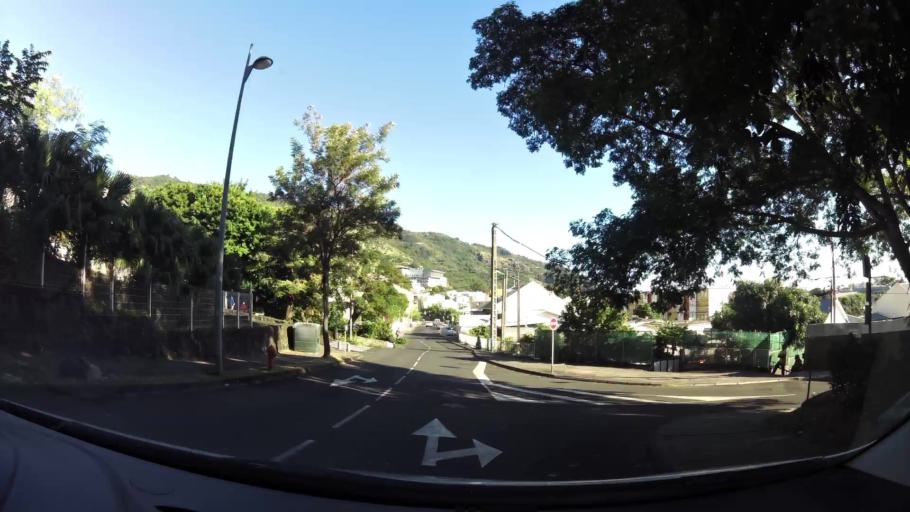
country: RE
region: Reunion
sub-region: Reunion
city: Saint-Denis
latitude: -20.8923
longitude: 55.4498
